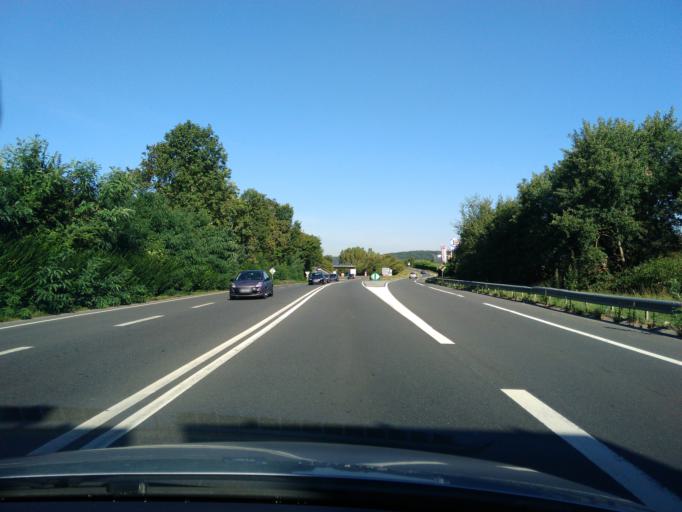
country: FR
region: Ile-de-France
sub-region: Departement de l'Essonne
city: Palaiseau
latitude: 48.7271
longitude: 2.2443
